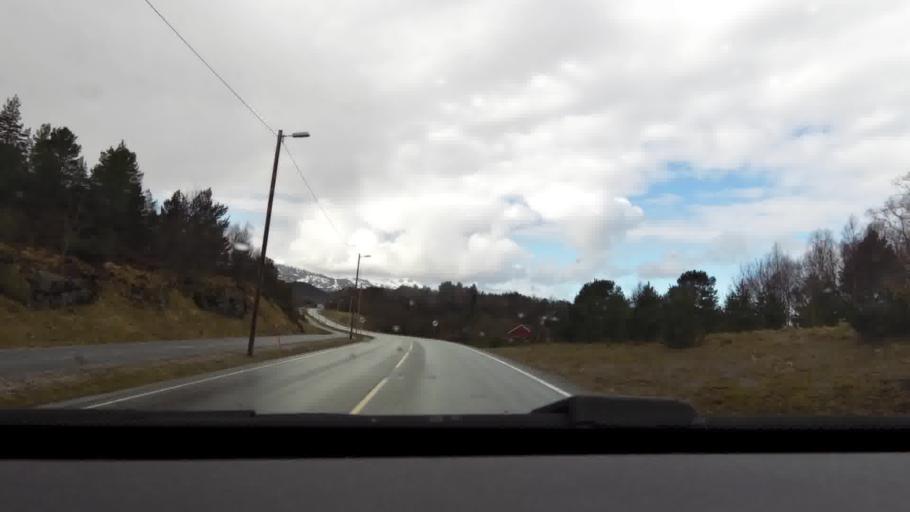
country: NO
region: More og Romsdal
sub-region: Eide
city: Eide
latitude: 62.9674
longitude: 7.3467
